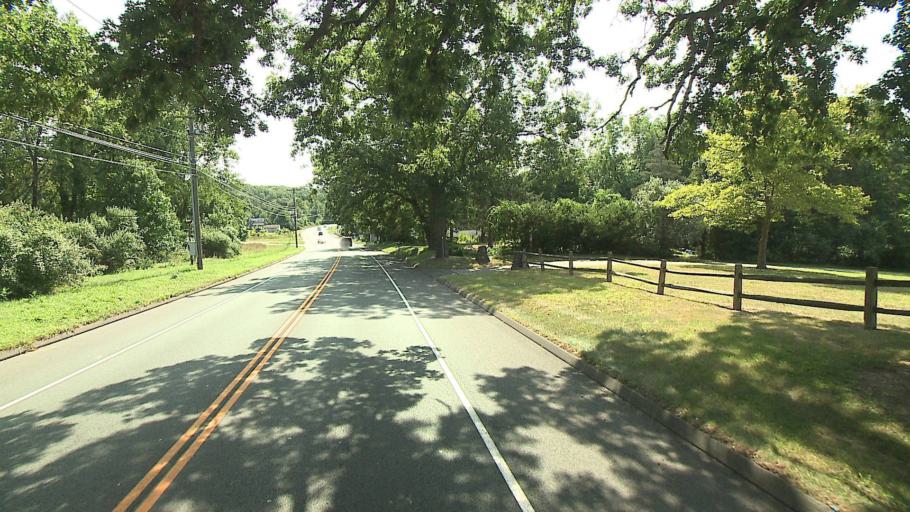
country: US
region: Connecticut
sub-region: Fairfield County
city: Newtown
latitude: 41.3770
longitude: -73.2758
